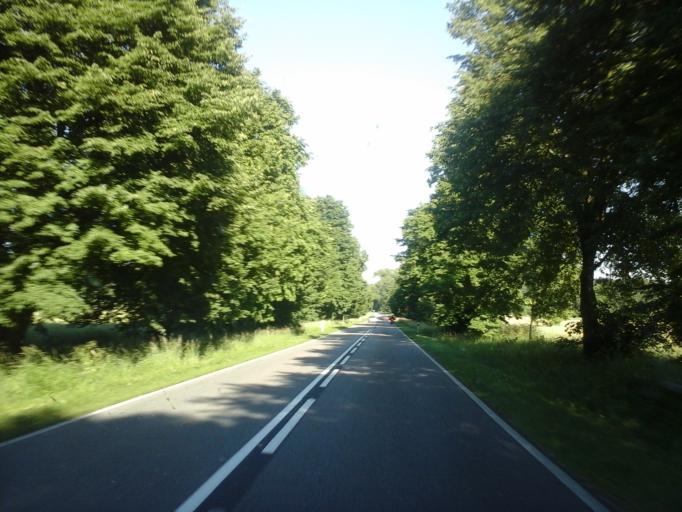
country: PL
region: West Pomeranian Voivodeship
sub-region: Powiat goleniowski
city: Nowogard
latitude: 53.6512
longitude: 15.2082
